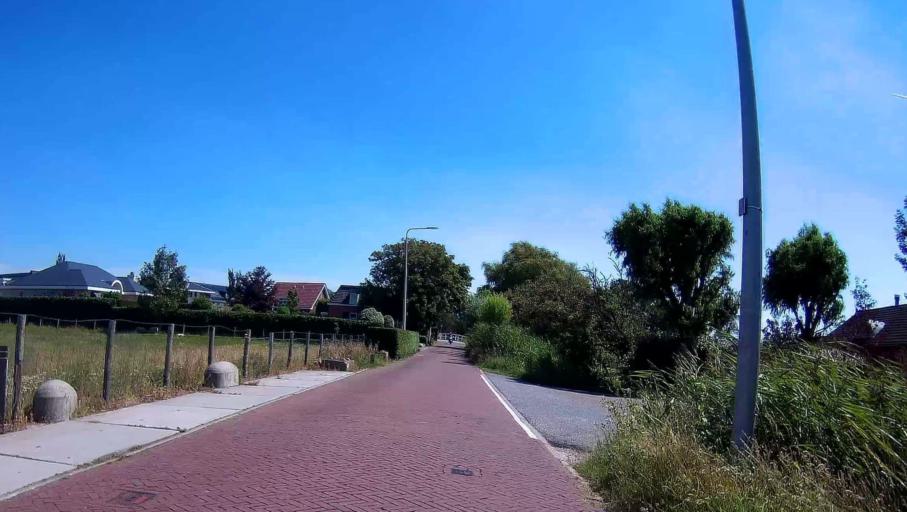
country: NL
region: South Holland
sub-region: Gemeente Westland
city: Naaldwijk
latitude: 51.9996
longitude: 4.1924
